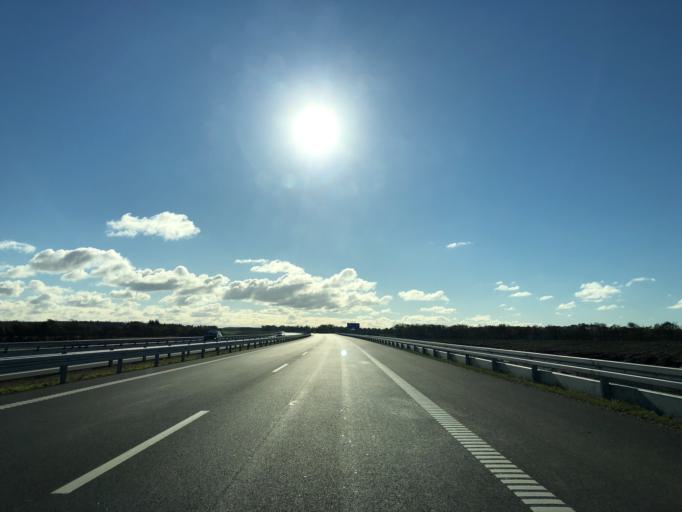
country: DK
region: Central Jutland
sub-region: Herning Kommune
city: Avlum
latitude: 56.3015
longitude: 8.7264
